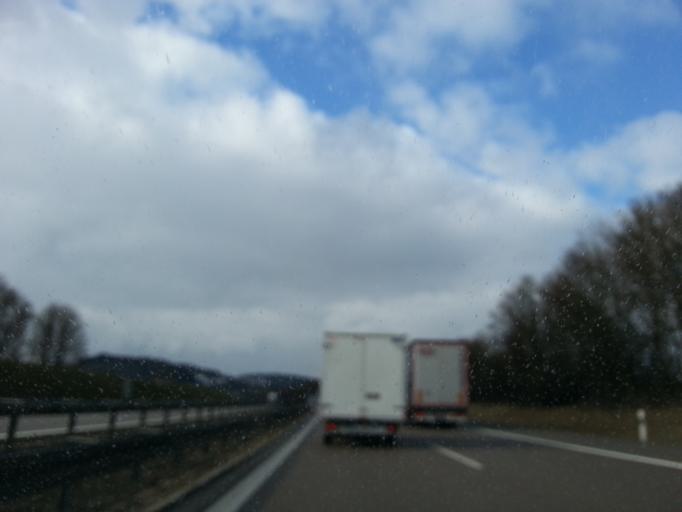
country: DE
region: Bavaria
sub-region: Upper Palatinate
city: Velburg
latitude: 49.2422
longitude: 11.6321
